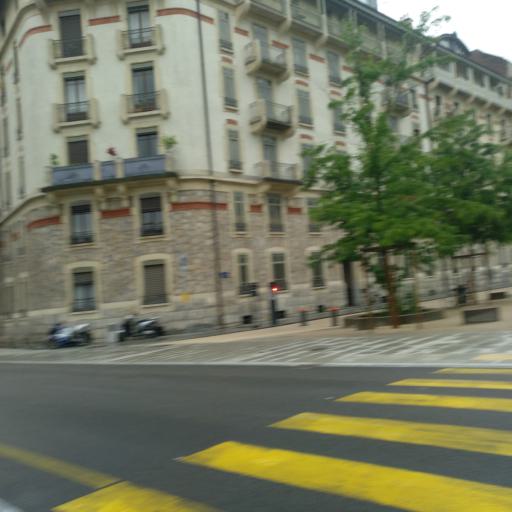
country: CH
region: Geneva
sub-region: Geneva
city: Le Grand-Saconnex
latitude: 46.2159
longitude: 6.1348
